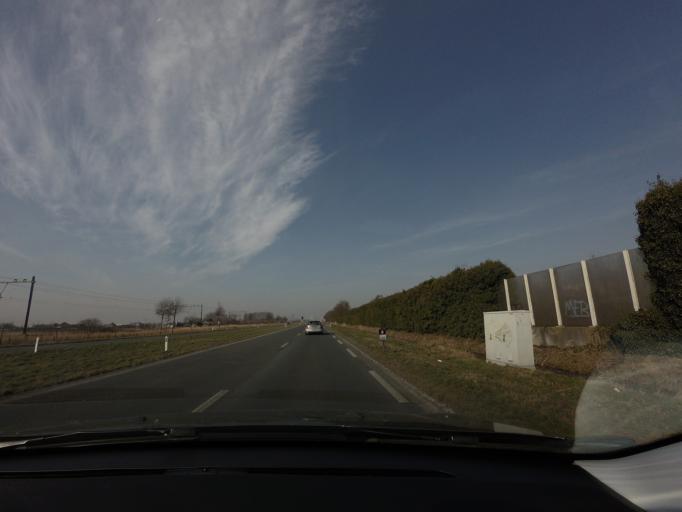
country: NL
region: North Holland
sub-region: Gemeente Uitgeest
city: Uitgeest
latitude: 52.4988
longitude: 4.7464
